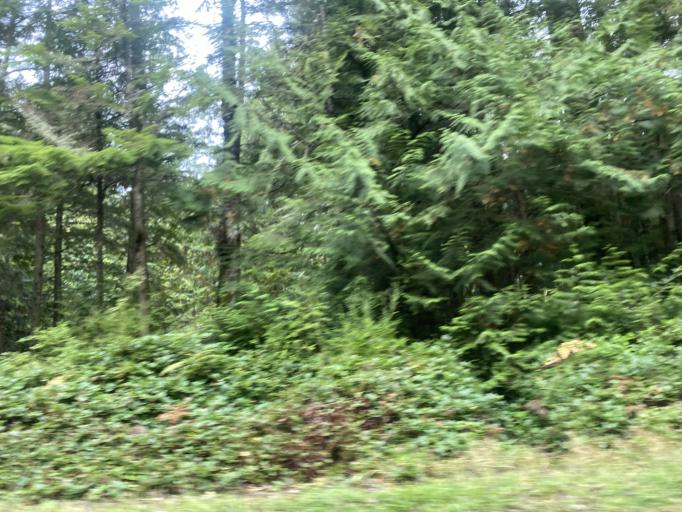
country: US
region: Washington
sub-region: Island County
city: Freeland
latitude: 48.0659
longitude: -122.4888
